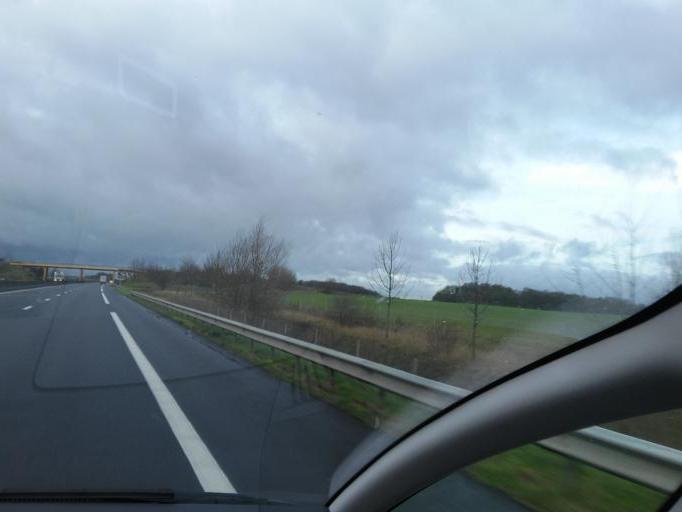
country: FR
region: Picardie
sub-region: Departement de la Somme
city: Boves
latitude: 49.8567
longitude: 2.4381
